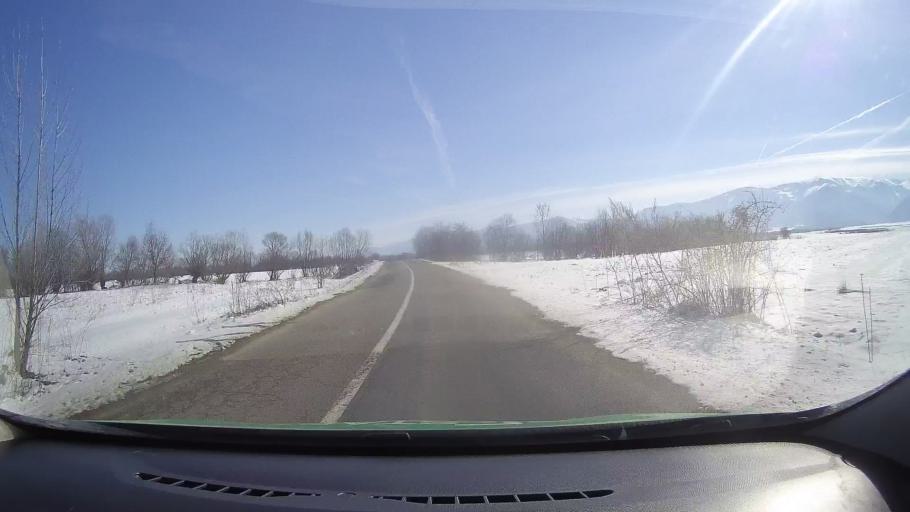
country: RO
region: Brasov
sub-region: Comuna Recea
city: Recea
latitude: 45.7297
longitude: 24.9690
